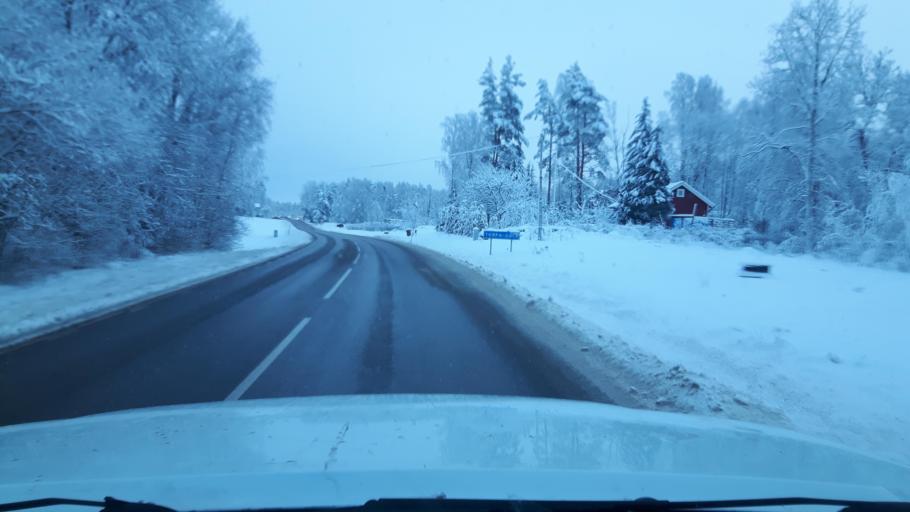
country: SE
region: Halland
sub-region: Kungsbacka Kommun
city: Fjaeras kyrkby
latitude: 57.4126
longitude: 12.2147
